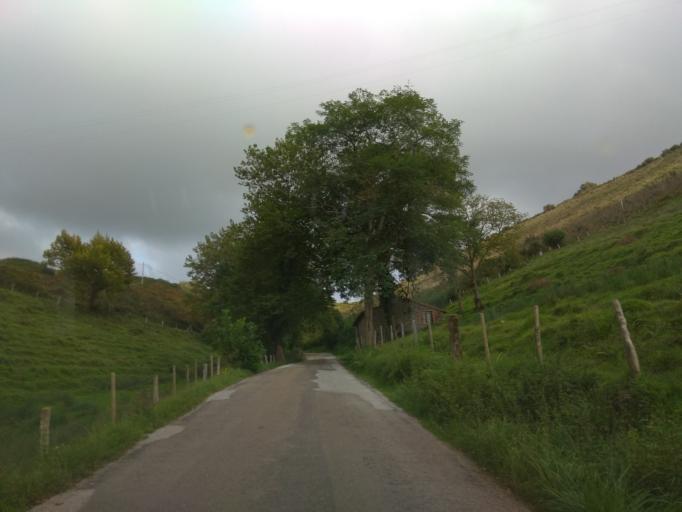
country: ES
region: Cantabria
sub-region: Provincia de Cantabria
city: San Vicente de la Barquera
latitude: 43.3138
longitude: -4.3898
